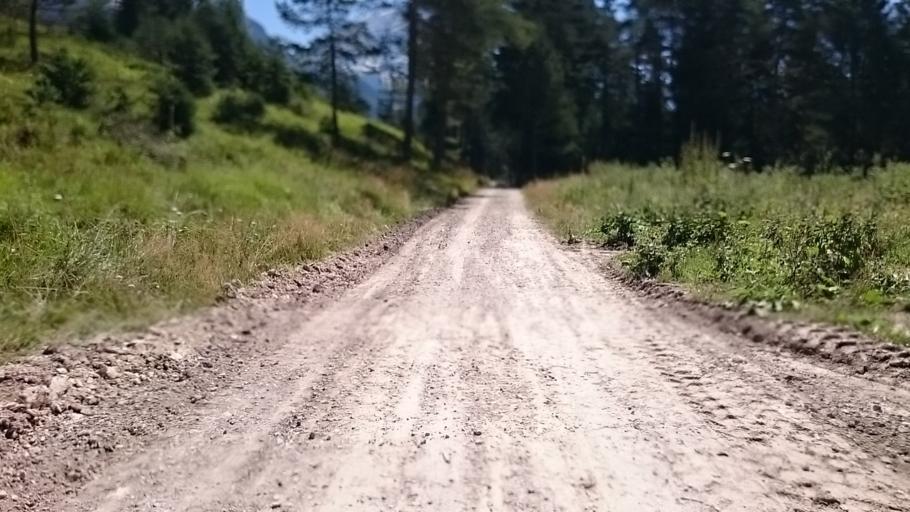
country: IT
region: Veneto
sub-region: Provincia di Belluno
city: Cortina d'Ampezzo
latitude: 46.4982
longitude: 12.1683
